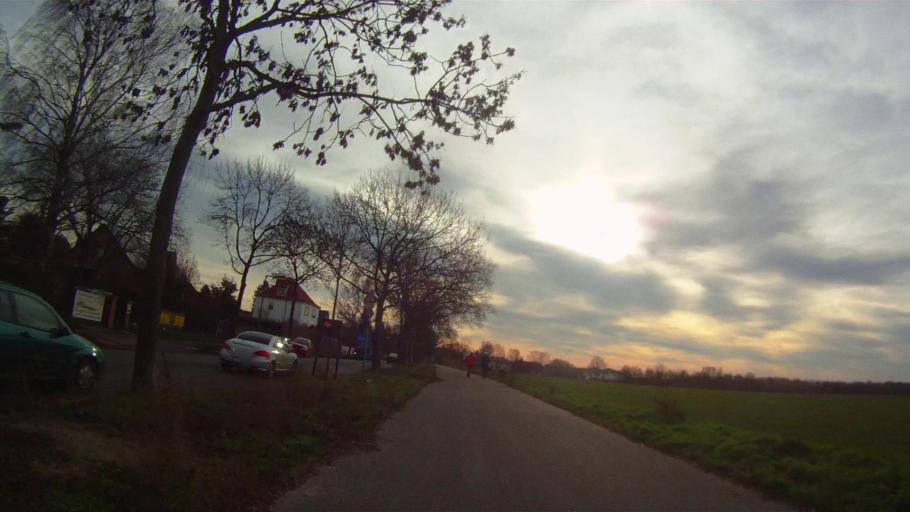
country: DE
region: Berlin
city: Britz
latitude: 52.4168
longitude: 13.4381
